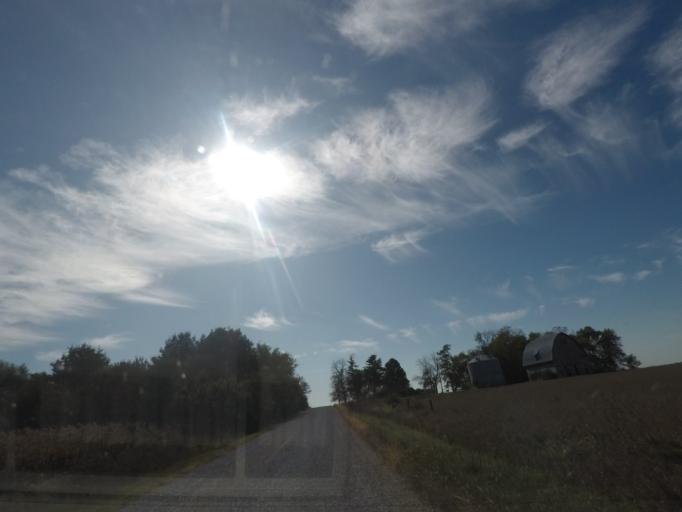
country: US
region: Iowa
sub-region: Story County
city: Nevada
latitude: 42.0509
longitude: -93.3290
